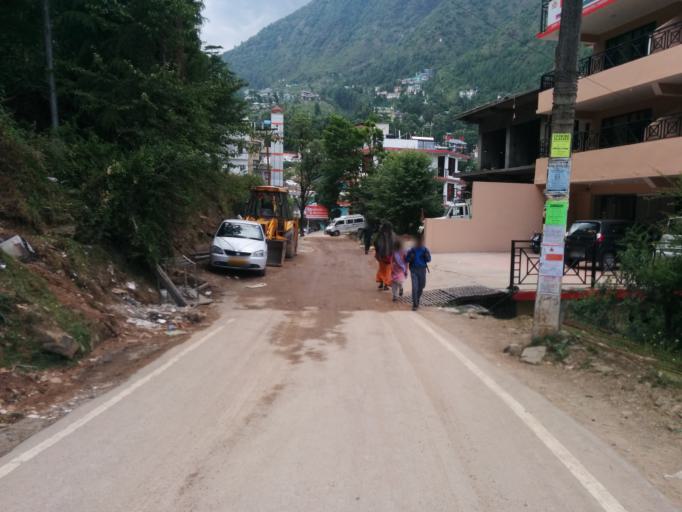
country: IN
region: Himachal Pradesh
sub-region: Kangra
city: Dharmsala
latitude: 32.2419
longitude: 76.3322
